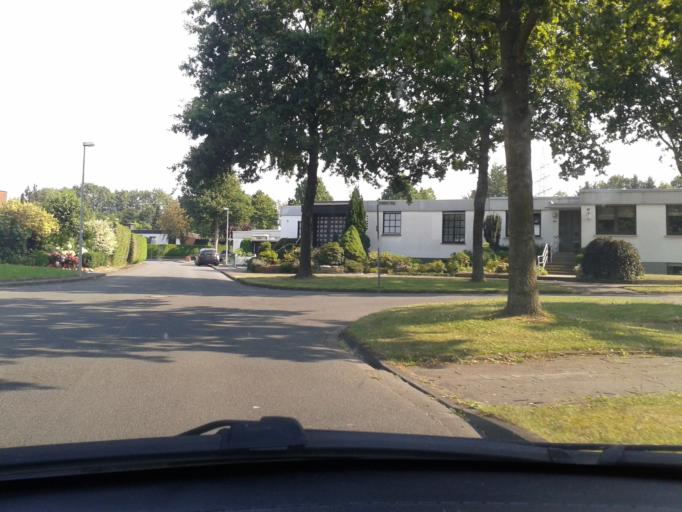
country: DE
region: North Rhine-Westphalia
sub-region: Regierungsbezirk Detmold
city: Paderborn
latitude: 51.7072
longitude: 8.7905
